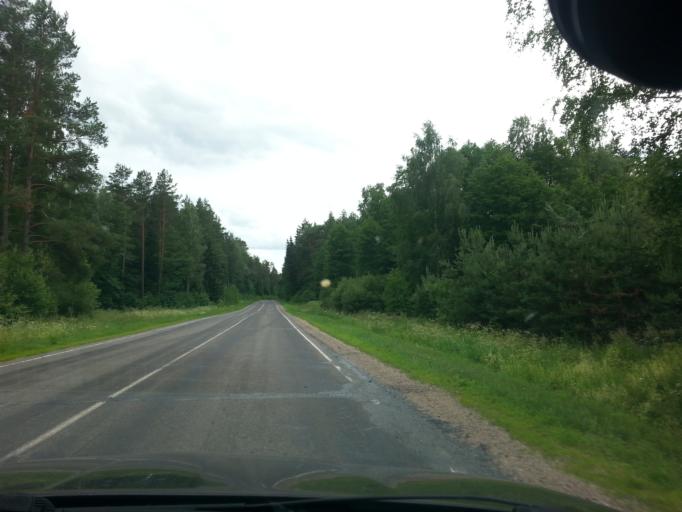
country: BY
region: Minsk
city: Svir
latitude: 54.8345
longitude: 26.1930
